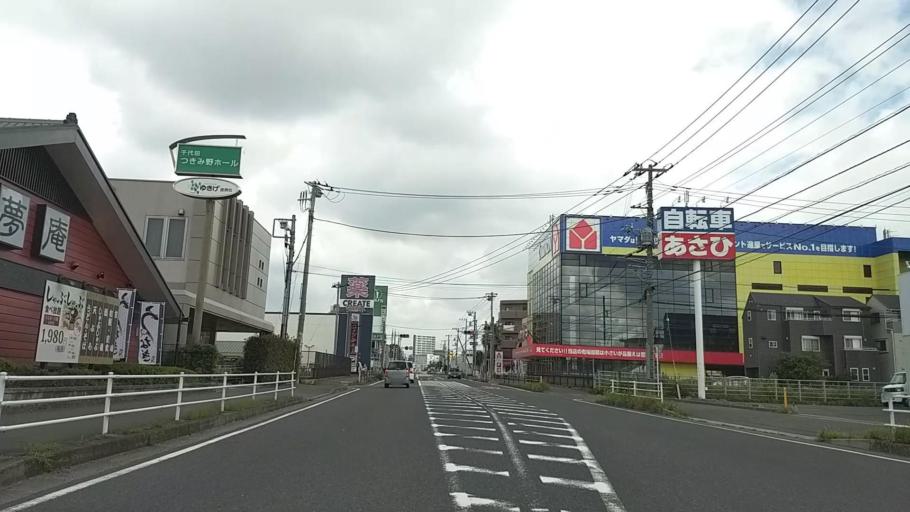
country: JP
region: Kanagawa
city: Minami-rinkan
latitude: 35.5104
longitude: 139.4601
